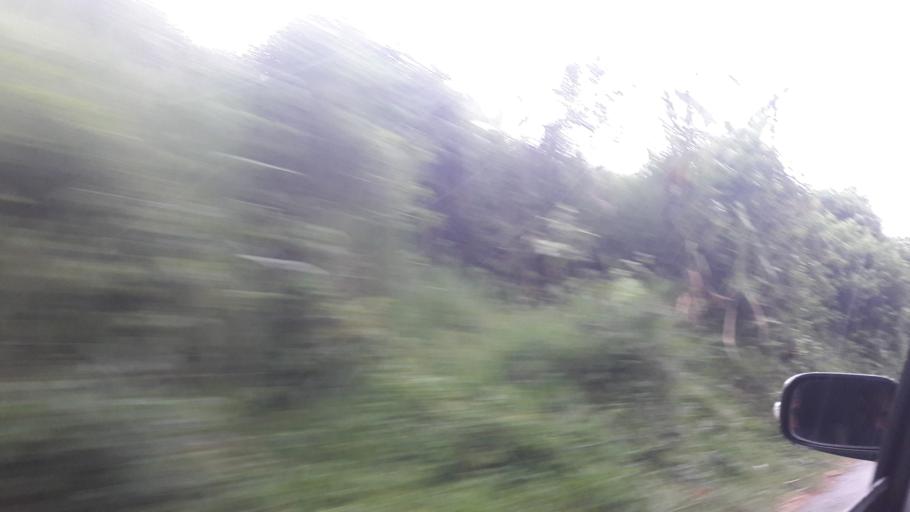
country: ID
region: West Java
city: Cipeundeuy
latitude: -6.6494
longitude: 106.5208
